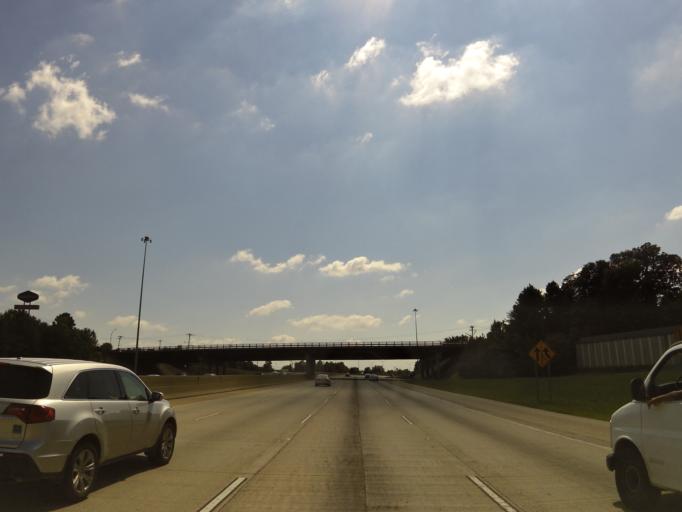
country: US
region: North Carolina
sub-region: Mecklenburg County
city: Charlotte
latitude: 35.2470
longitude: -80.8968
